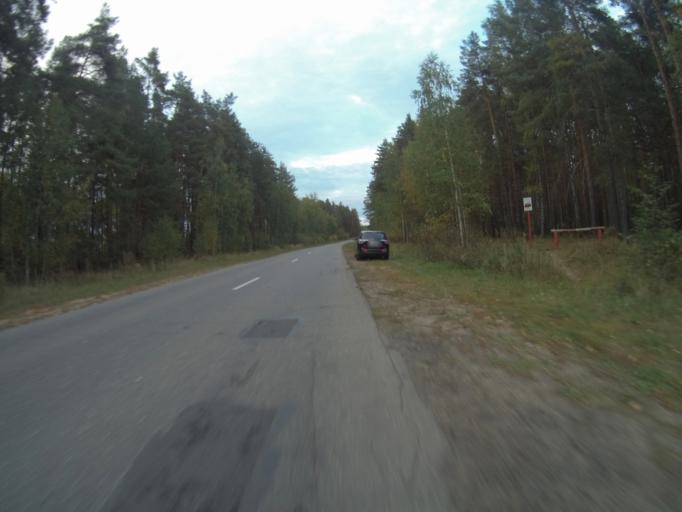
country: RU
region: Vladimir
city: Vorsha
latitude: 56.0082
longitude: 40.0983
